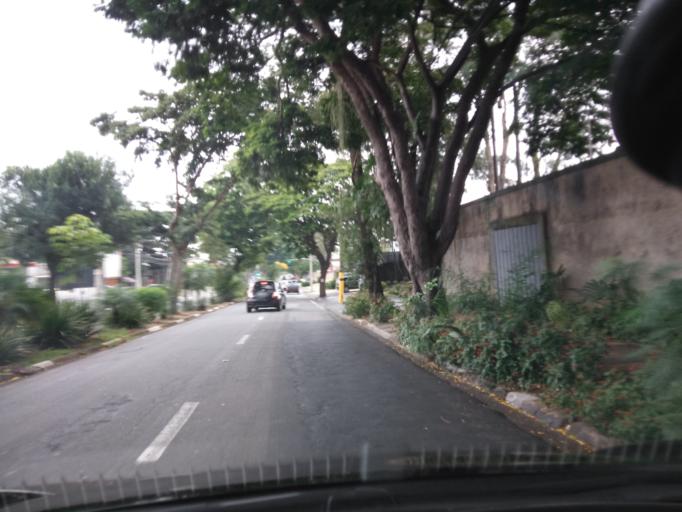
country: BR
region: Sao Paulo
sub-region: Campinas
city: Campinas
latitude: -22.8977
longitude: -47.0299
